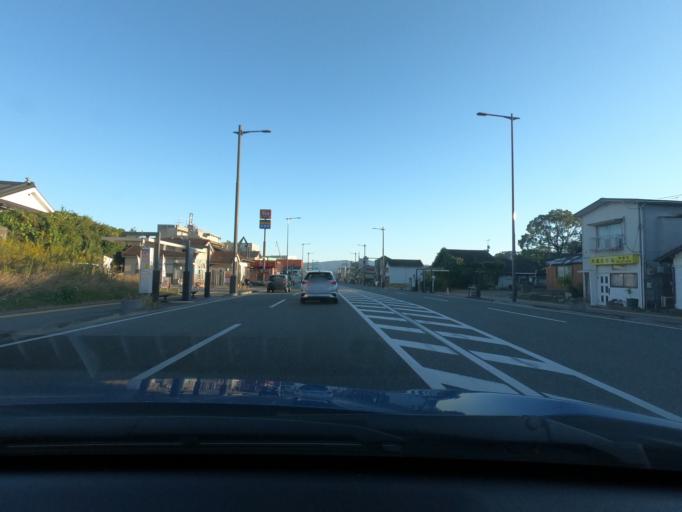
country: JP
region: Kagoshima
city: Satsumasendai
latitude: 31.8310
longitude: 130.2957
